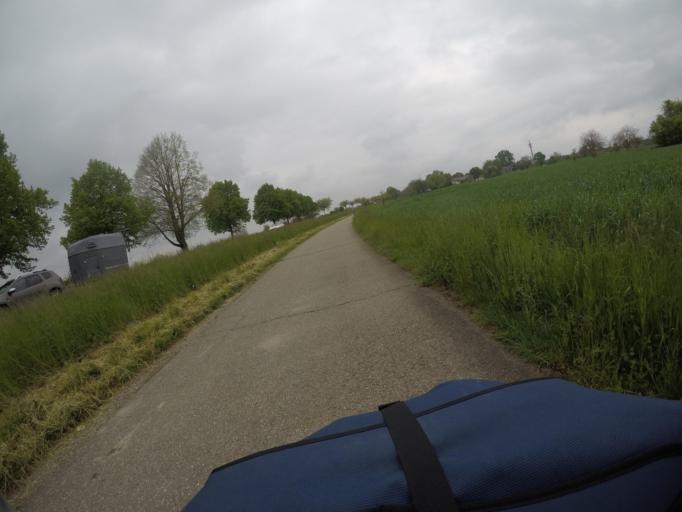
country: DE
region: Baden-Wuerttemberg
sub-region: Karlsruhe Region
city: Iffezheim
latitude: 48.8511
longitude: 8.1411
